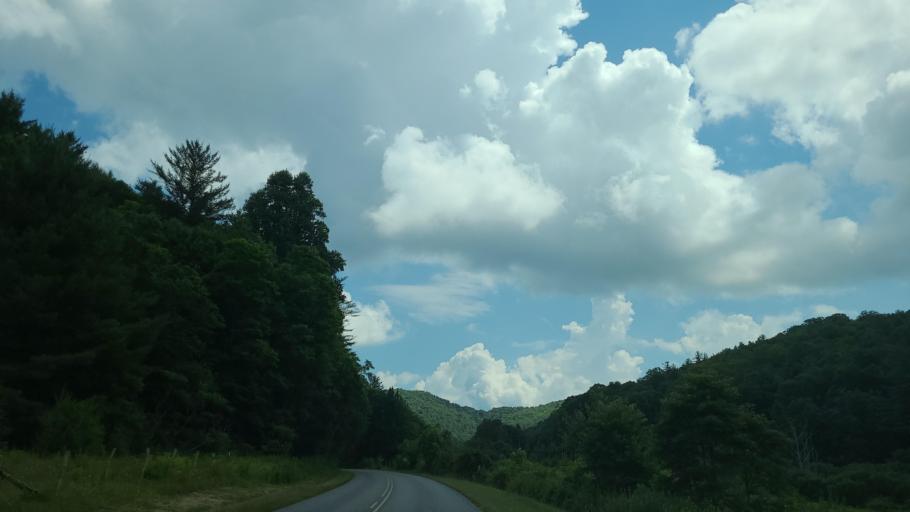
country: US
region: North Carolina
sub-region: Avery County
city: Newland
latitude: 35.9819
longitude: -81.9128
